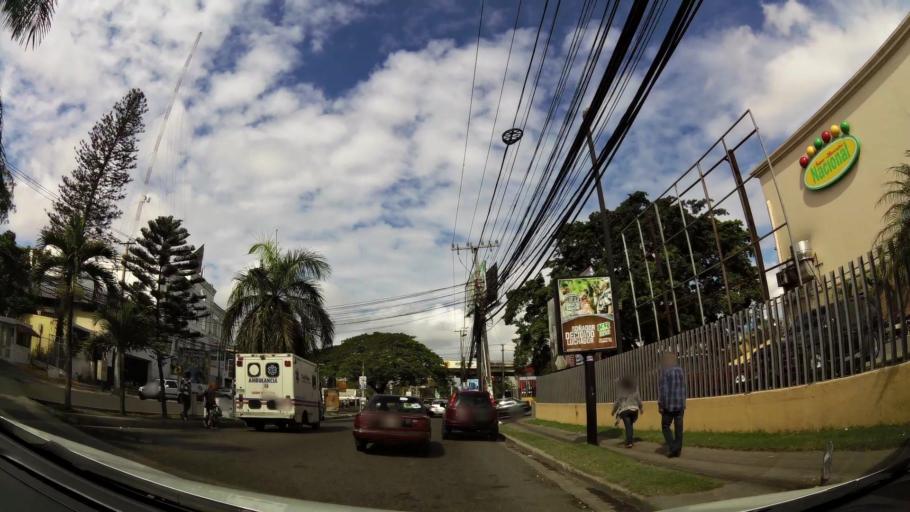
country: DO
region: Santiago
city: Santiago de los Caballeros
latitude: 19.4608
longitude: -70.6851
